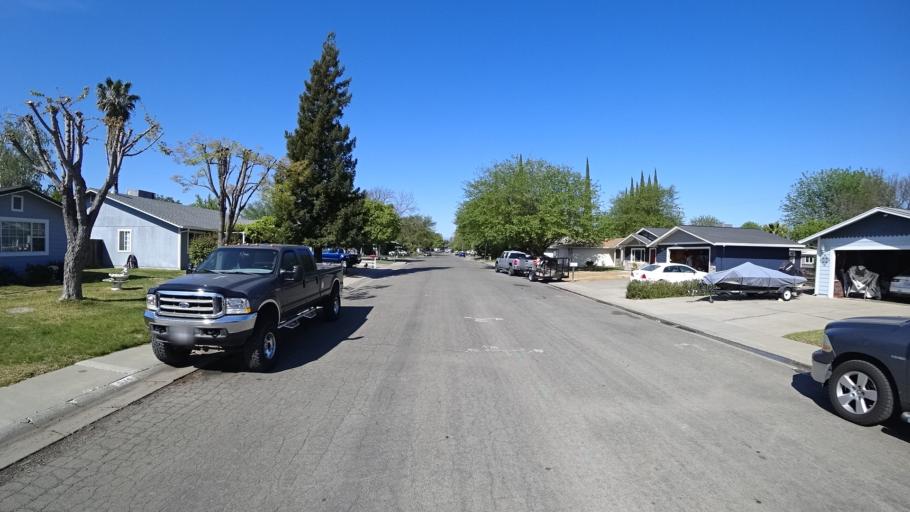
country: US
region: California
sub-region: Glenn County
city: Willows
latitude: 39.5302
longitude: -122.1999
